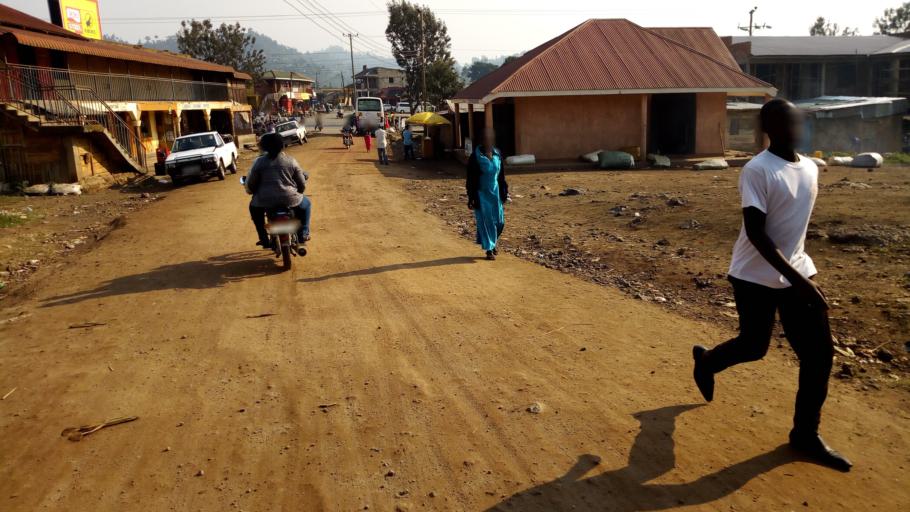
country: UG
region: Western Region
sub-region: Kisoro District
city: Kisoro
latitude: -1.2831
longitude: 29.6959
